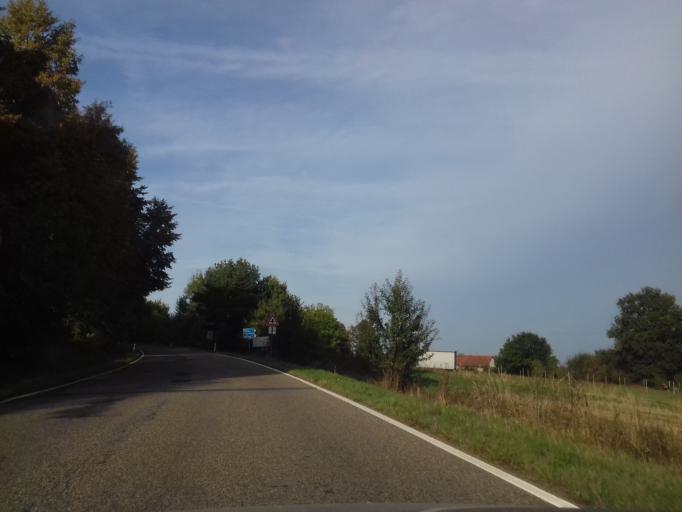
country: CZ
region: Central Bohemia
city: Netvorice
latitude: 49.8119
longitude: 14.5130
